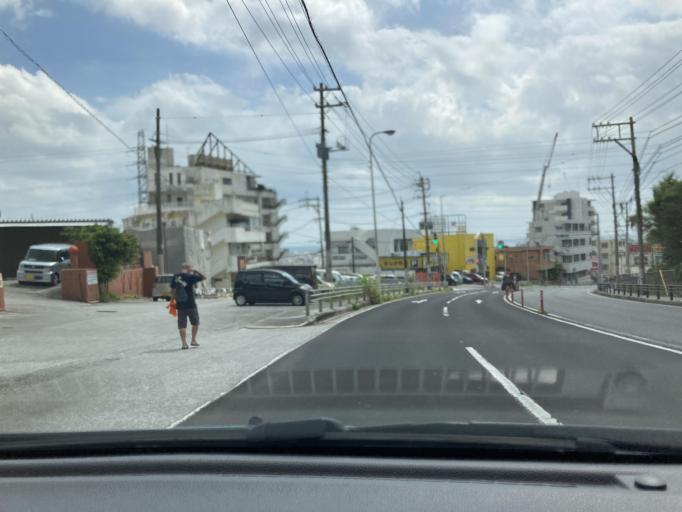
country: JP
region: Okinawa
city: Okinawa
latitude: 26.3315
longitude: 127.8222
